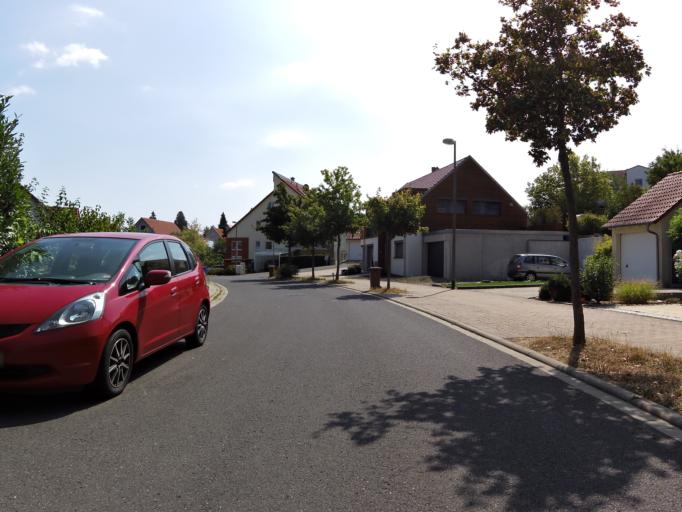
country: DE
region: Bavaria
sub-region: Regierungsbezirk Unterfranken
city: Zell am Main
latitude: 49.8129
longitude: 9.8638
